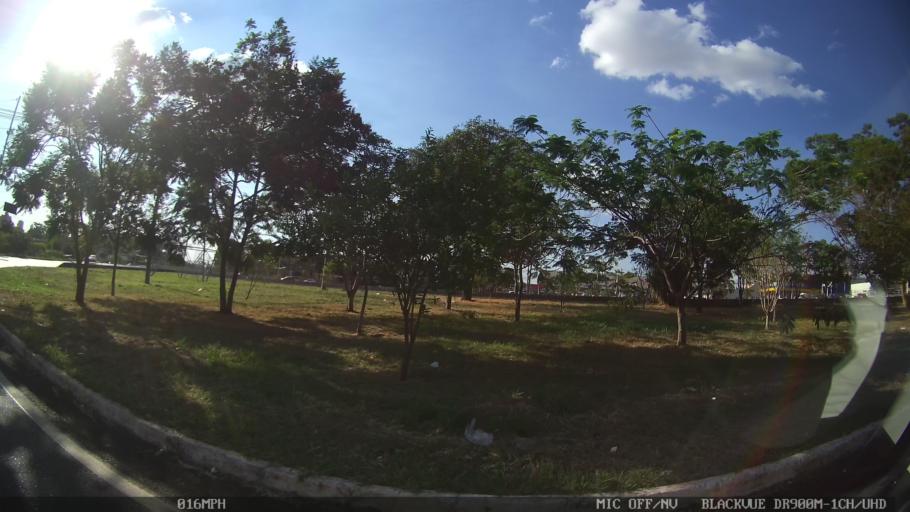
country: BR
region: Sao Paulo
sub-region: Ribeirao Preto
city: Ribeirao Preto
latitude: -21.1941
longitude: -47.7765
